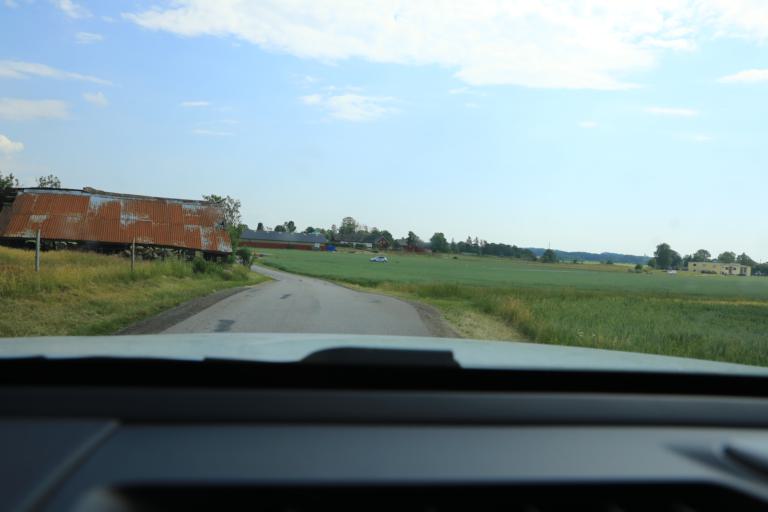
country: SE
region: Halland
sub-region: Varbergs Kommun
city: Varberg
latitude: 57.1357
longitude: 12.3273
